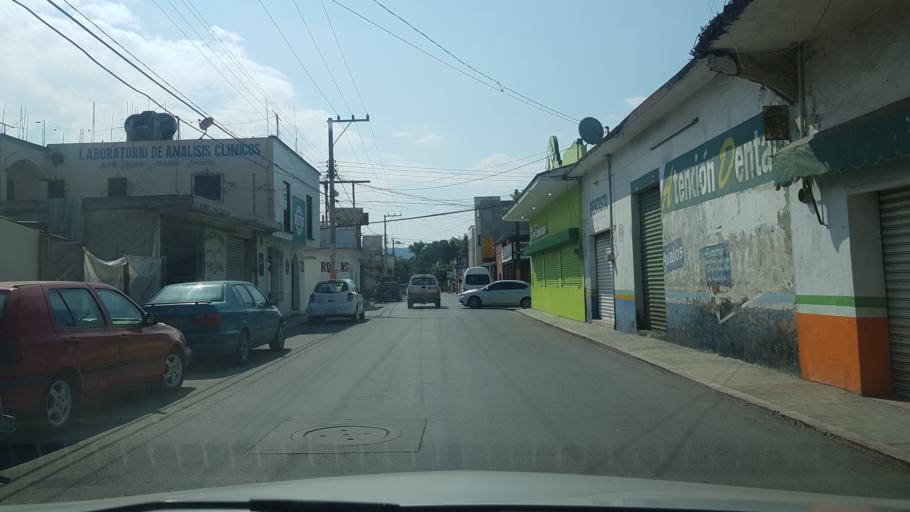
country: MX
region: Morelos
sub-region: Jojutla
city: Jojutla
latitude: 18.6185
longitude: -99.1801
